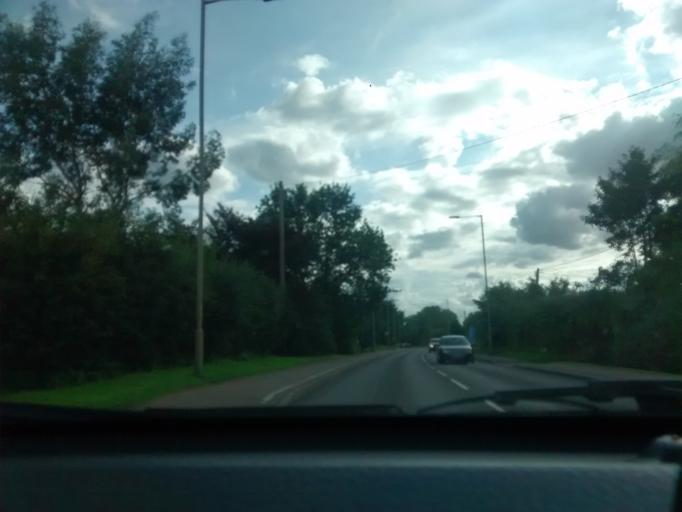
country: GB
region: England
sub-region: Norfolk
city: King's Lynn
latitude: 52.7317
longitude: 0.4169
